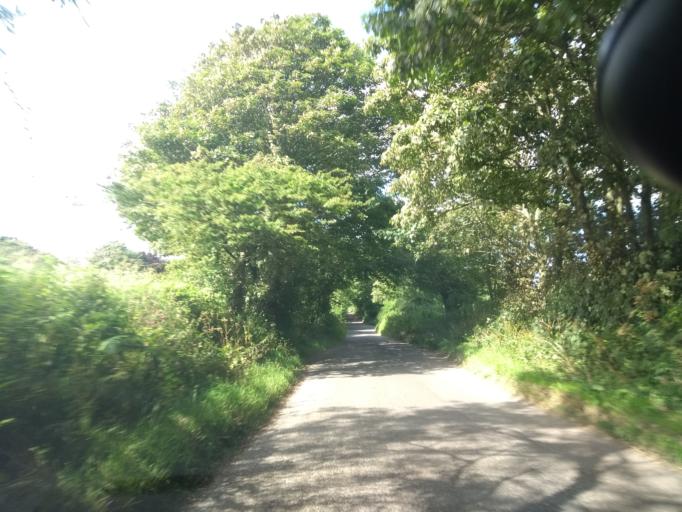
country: GB
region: England
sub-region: Devon
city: Modbury
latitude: 50.3045
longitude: -3.8860
